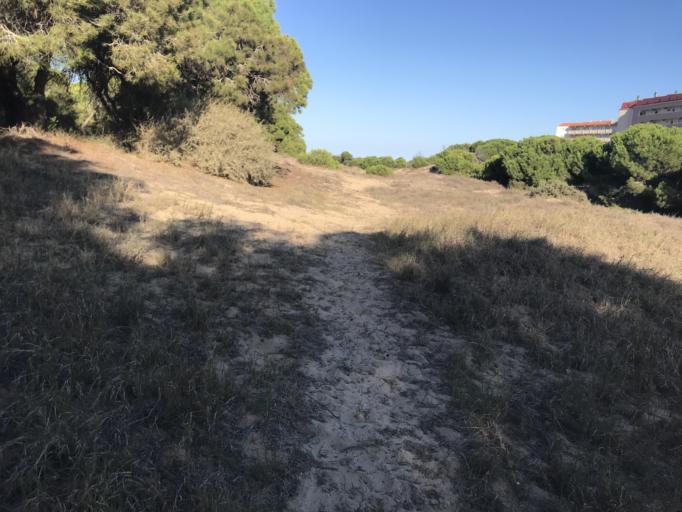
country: ES
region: Valencia
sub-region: Provincia de Alicante
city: Guardamar del Segura
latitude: 38.0315
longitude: -0.6562
